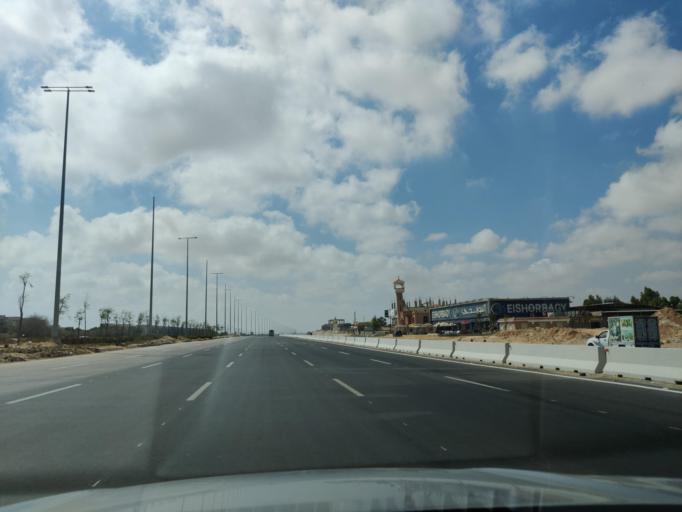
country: EG
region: Muhafazat Matruh
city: Al `Alamayn
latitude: 30.9422
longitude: 28.7809
